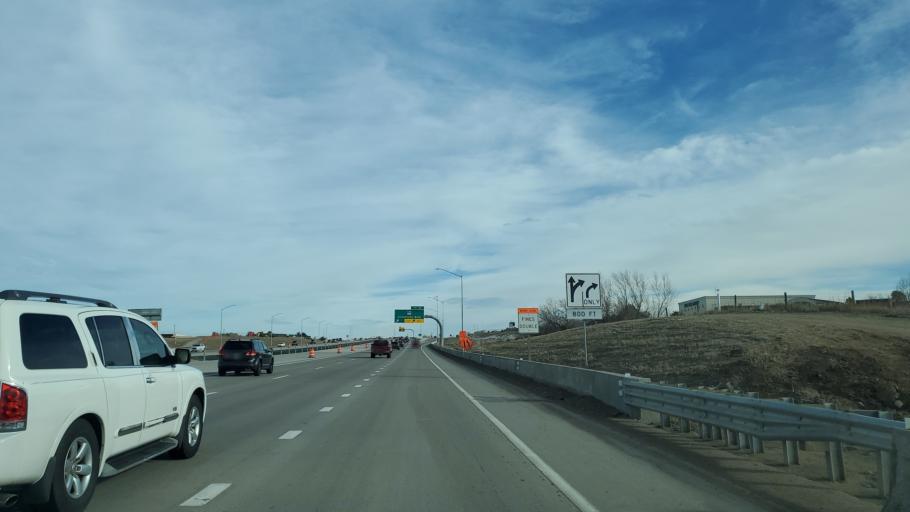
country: US
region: Colorado
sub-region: Douglas County
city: Highlands Ranch
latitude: 39.5639
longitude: -104.9699
